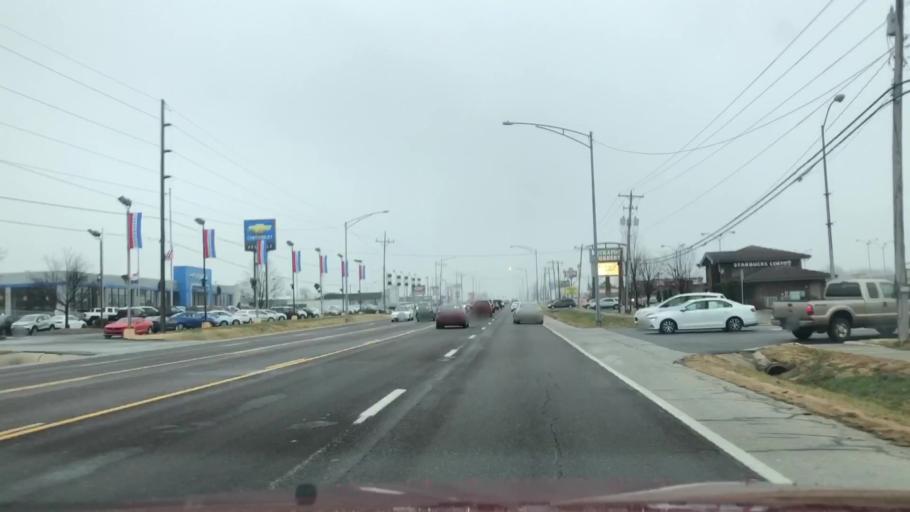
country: US
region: Missouri
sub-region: Greene County
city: Springfield
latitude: 37.1470
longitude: -93.2959
